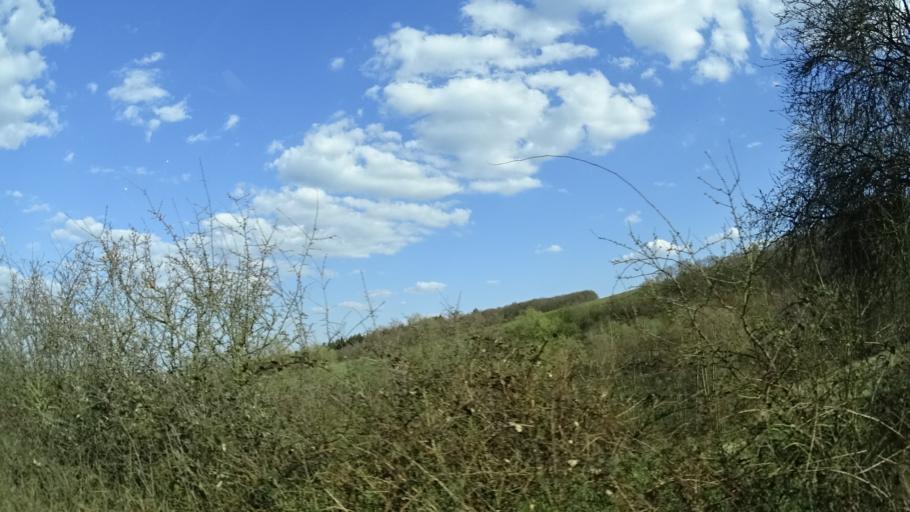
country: DE
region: Rheinland-Pfalz
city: Kirschroth
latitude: 49.7551
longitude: 7.5710
